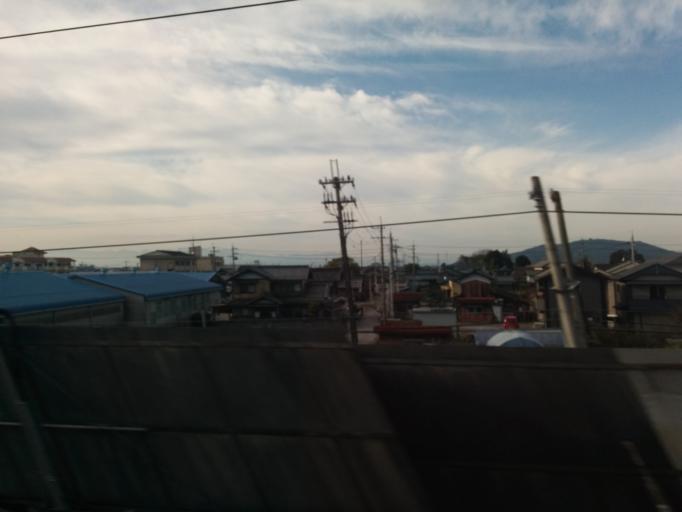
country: JP
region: Shiga Prefecture
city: Hikone
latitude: 35.2000
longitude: 136.2333
